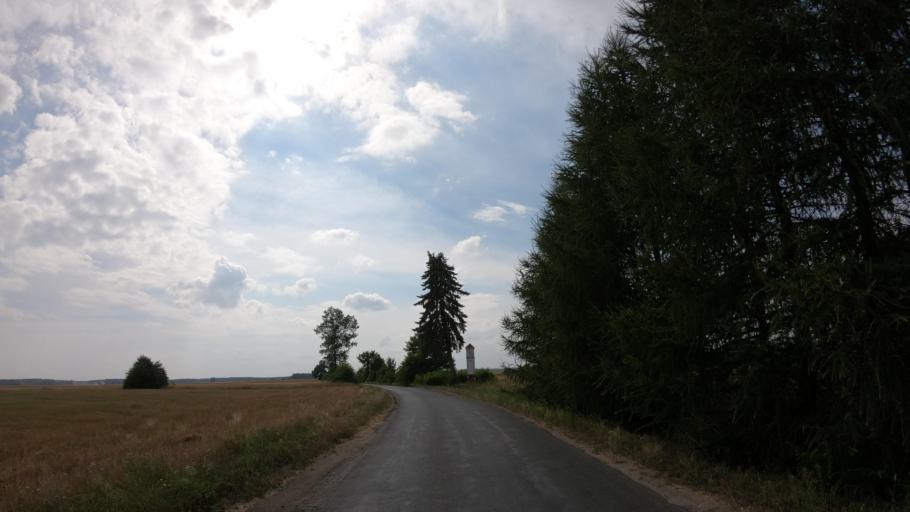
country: PL
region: West Pomeranian Voivodeship
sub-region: Powiat walecki
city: Tuczno
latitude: 53.2467
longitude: 16.1299
